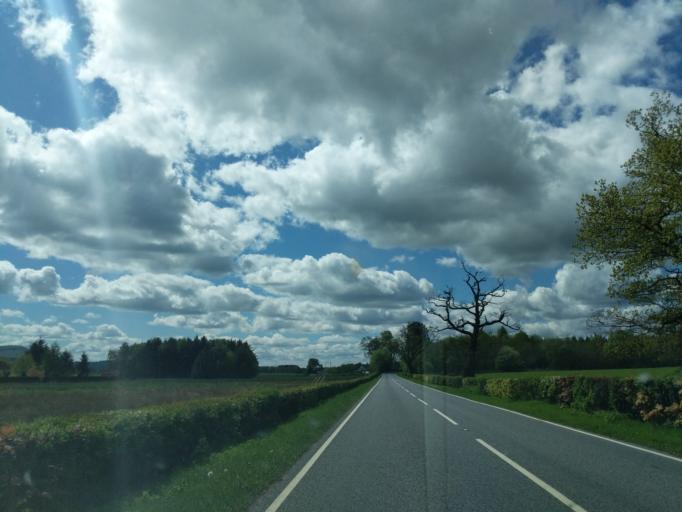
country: GB
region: Scotland
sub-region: Stirling
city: Doune
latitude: 56.1624
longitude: -4.0655
